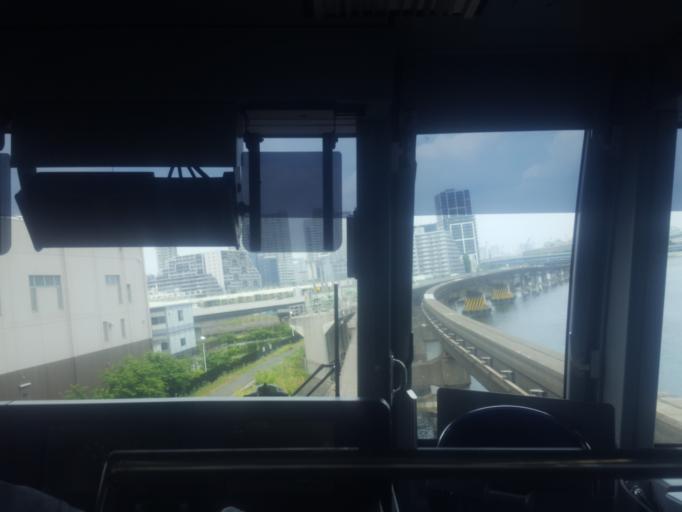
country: JP
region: Kanagawa
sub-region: Kawasaki-shi
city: Kawasaki
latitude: 35.6005
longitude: 139.7474
